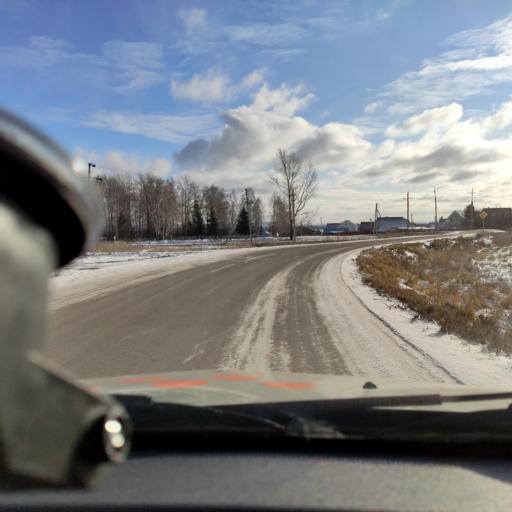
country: RU
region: Bashkortostan
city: Mikhaylovka
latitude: 54.8078
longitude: 55.7887
